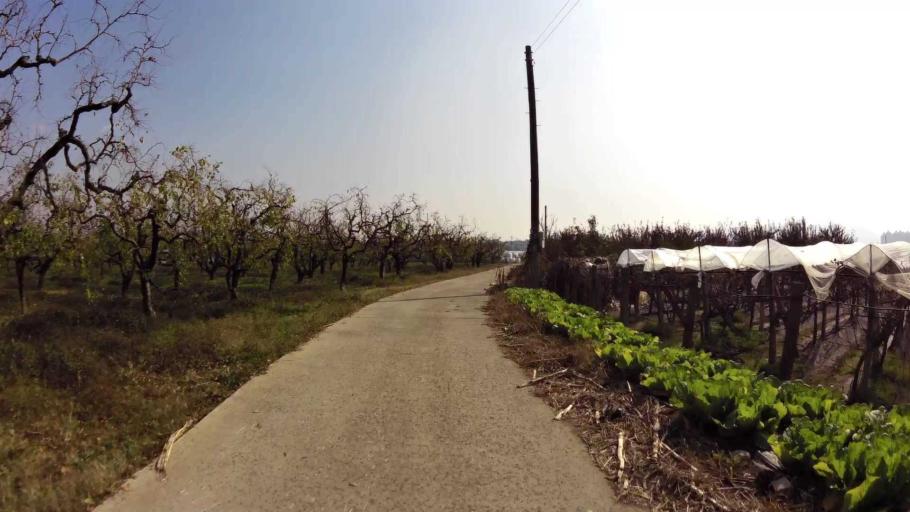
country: KR
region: Gyeongsangbuk-do
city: Gyeongsan-si
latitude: 35.8492
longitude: 128.7410
